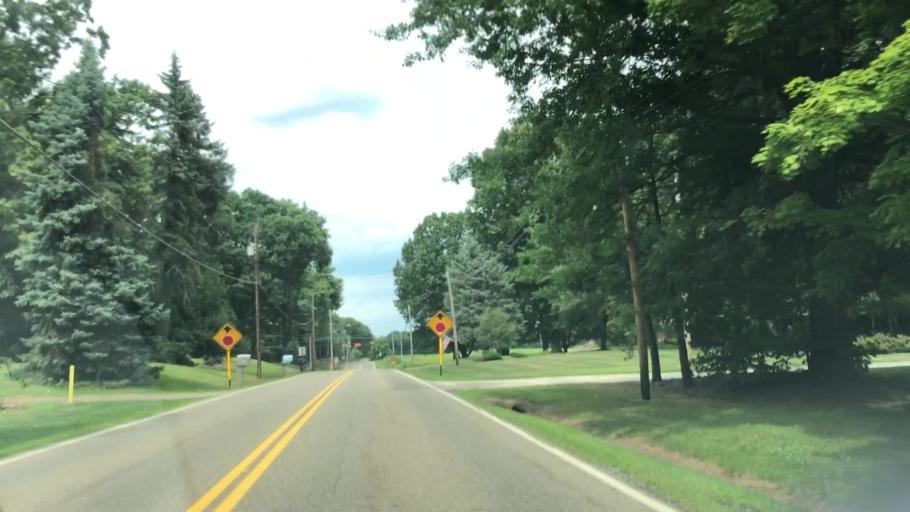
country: US
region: Ohio
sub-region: Summit County
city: Greensburg
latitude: 40.8913
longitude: -81.4594
